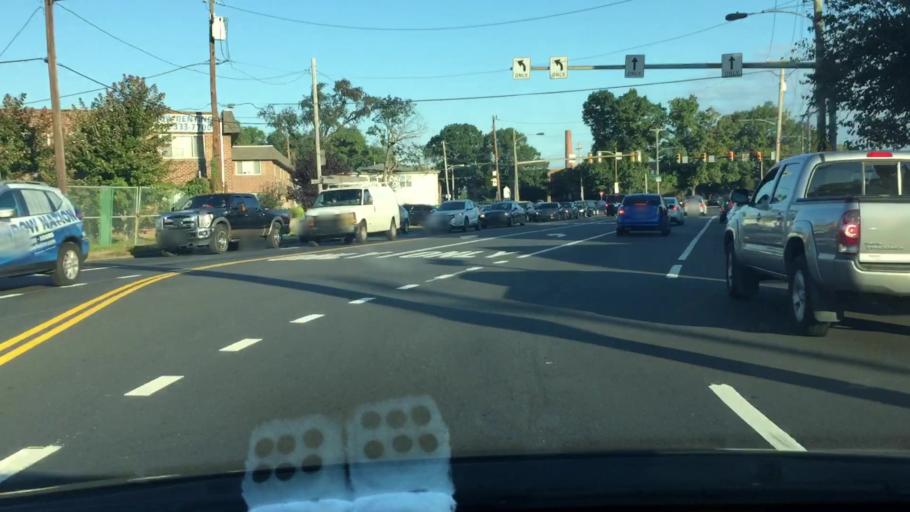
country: US
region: New Jersey
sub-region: Burlington County
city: Riverton
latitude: 40.0527
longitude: -75.0083
